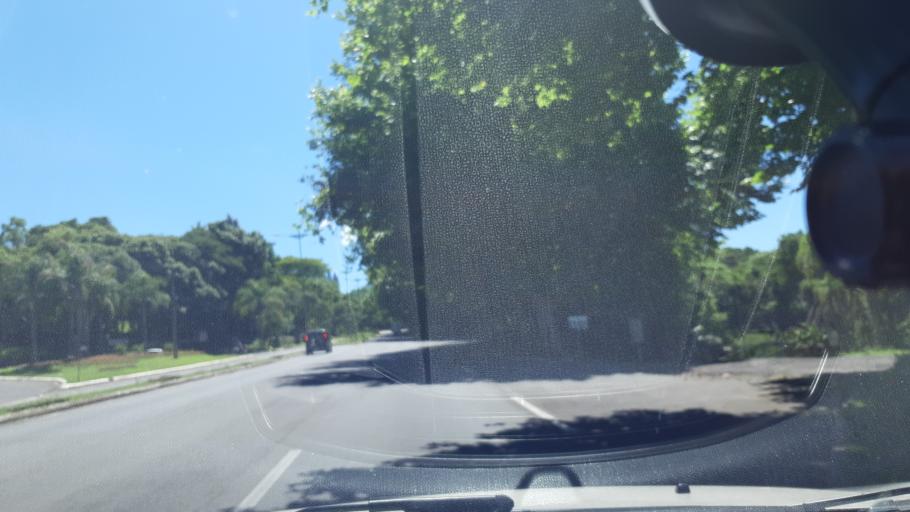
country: BR
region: Rio Grande do Sul
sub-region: Ivoti
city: Ivoti
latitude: -29.6256
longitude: -51.1365
